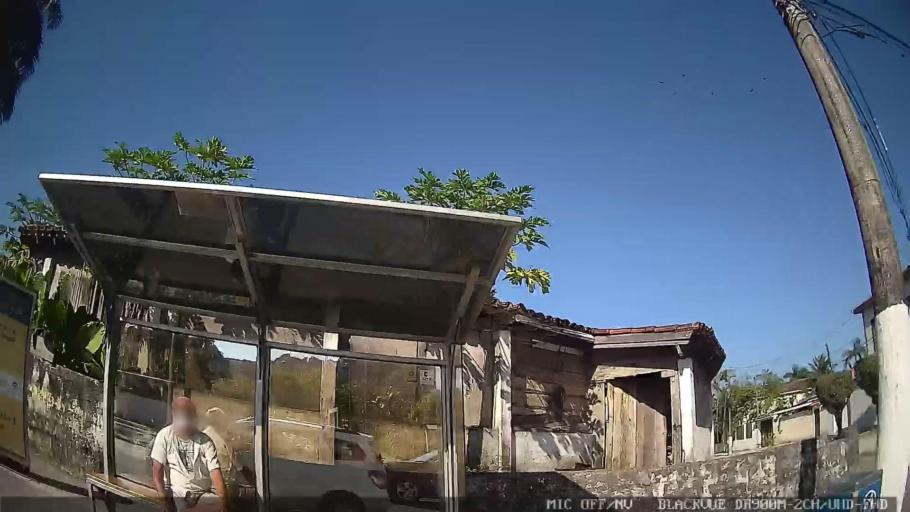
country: BR
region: Sao Paulo
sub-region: Guaruja
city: Guaruja
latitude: -24.0131
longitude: -46.2807
